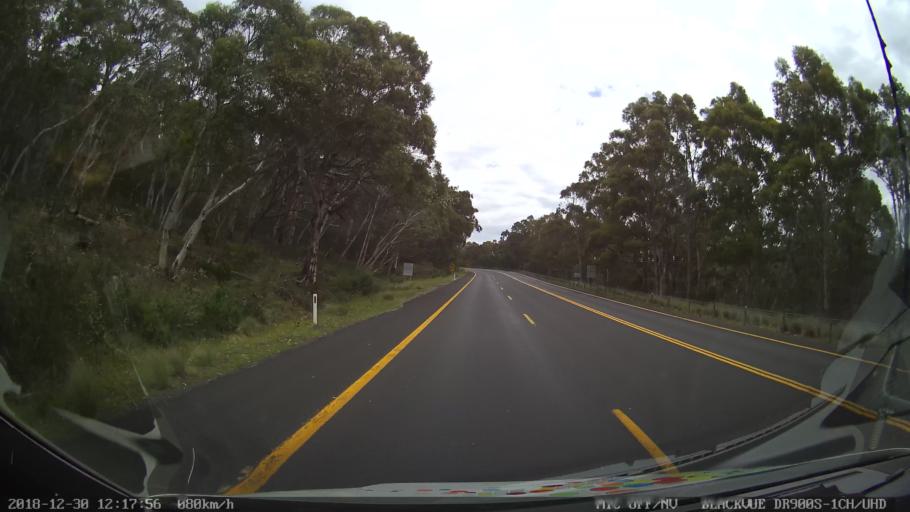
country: AU
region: New South Wales
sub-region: Snowy River
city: Jindabyne
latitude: -36.3515
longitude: 148.5539
